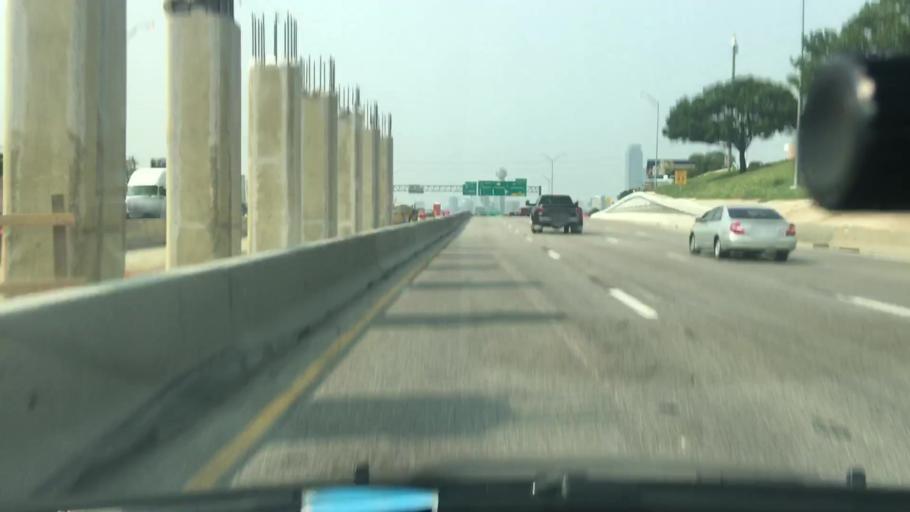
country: US
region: Texas
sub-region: Dallas County
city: Dallas
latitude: 32.7510
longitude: -96.8088
